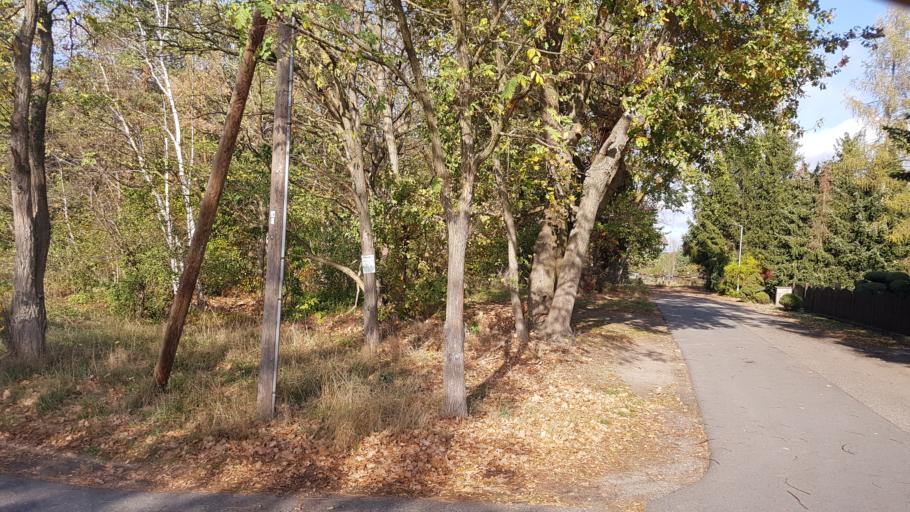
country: DE
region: Brandenburg
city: Ruckersdorf
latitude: 51.5701
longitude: 13.5731
